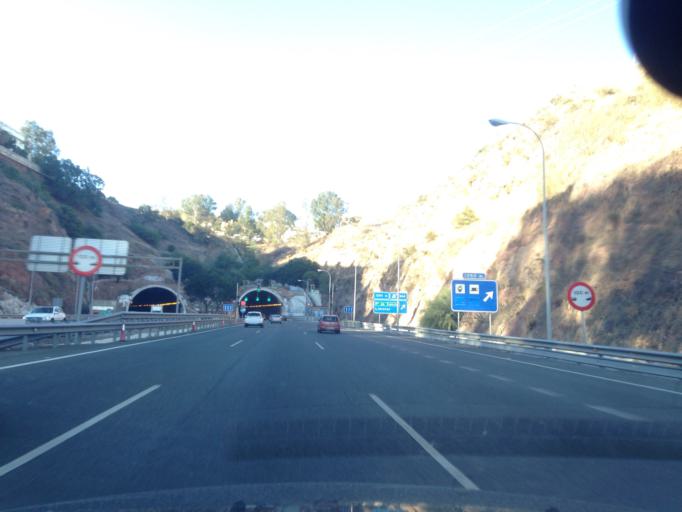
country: ES
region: Andalusia
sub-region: Provincia de Malaga
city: Malaga
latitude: 36.7355
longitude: -4.3773
